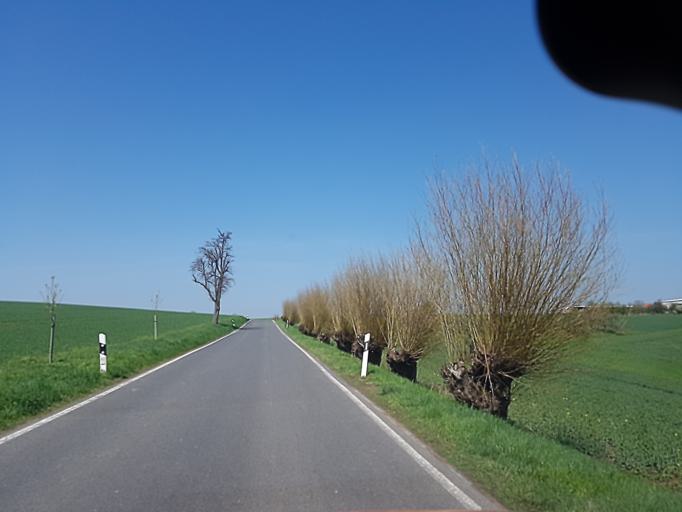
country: DE
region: Saxony
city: Bockelwitz
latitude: 51.1710
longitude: 12.9789
